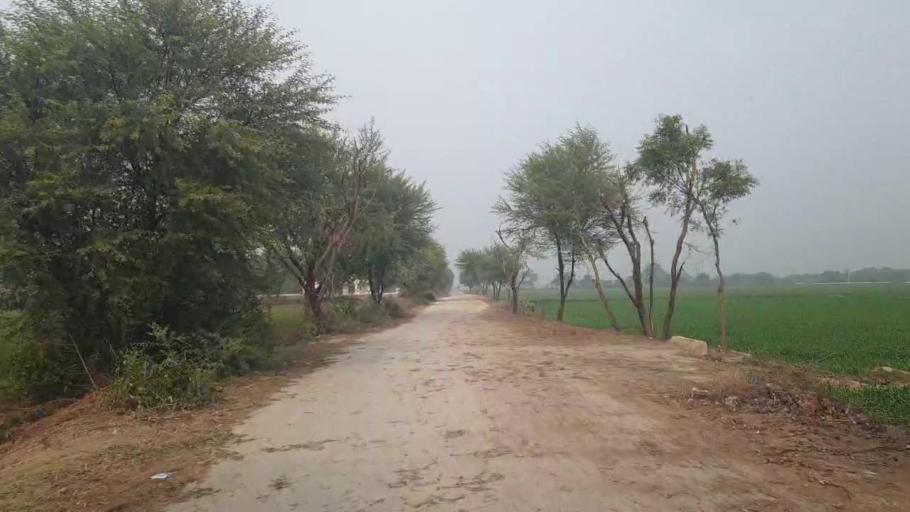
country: PK
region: Sindh
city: Tando Adam
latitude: 25.7669
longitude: 68.7025
